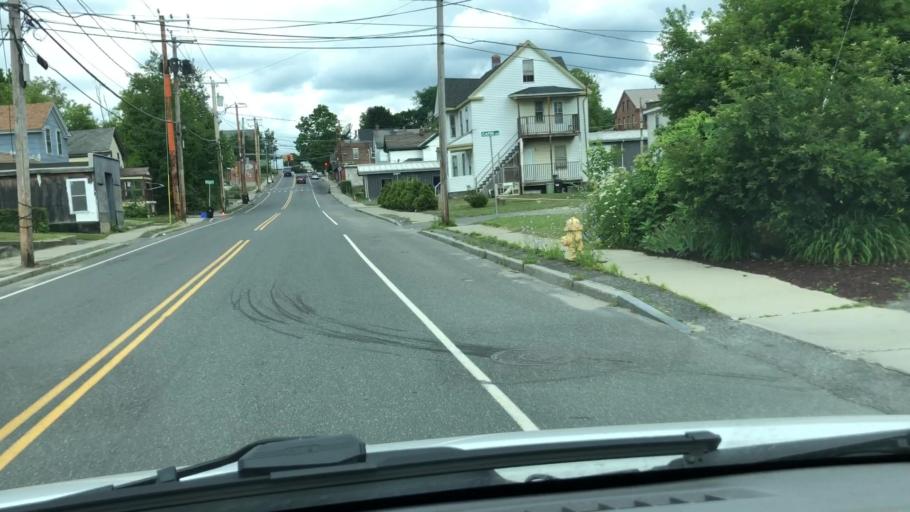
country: US
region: Massachusetts
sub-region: Berkshire County
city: Pittsfield
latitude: 42.4488
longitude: -73.2430
